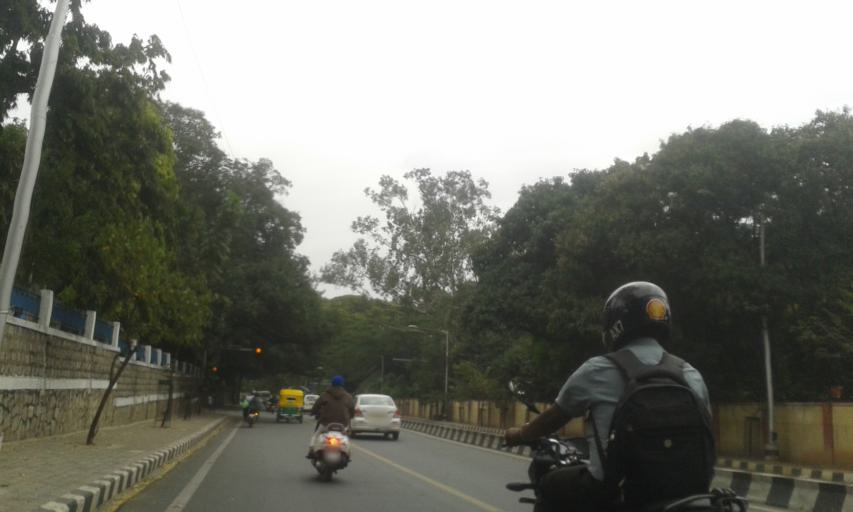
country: IN
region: Karnataka
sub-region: Bangalore Urban
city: Bangalore
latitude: 12.9631
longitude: 77.6271
